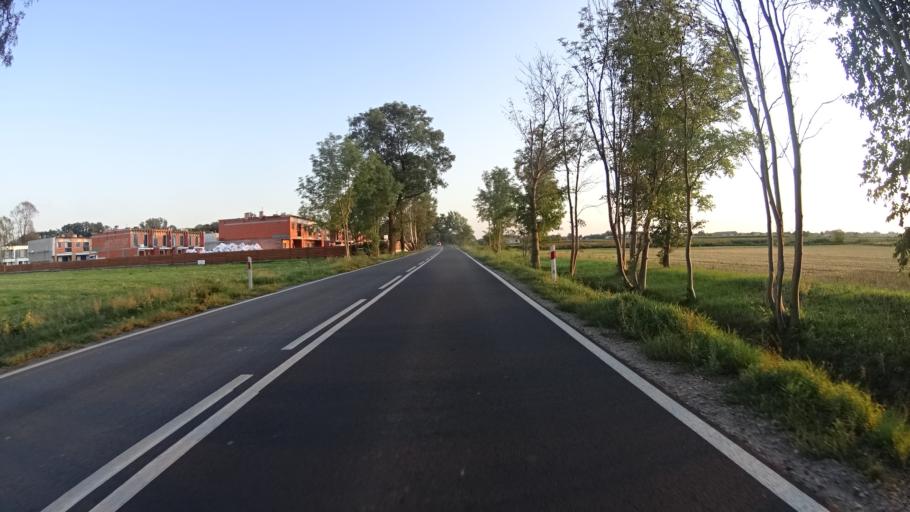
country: PL
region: Masovian Voivodeship
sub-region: Powiat warszawski zachodni
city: Ozarow Mazowiecki
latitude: 52.2211
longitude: 20.7735
